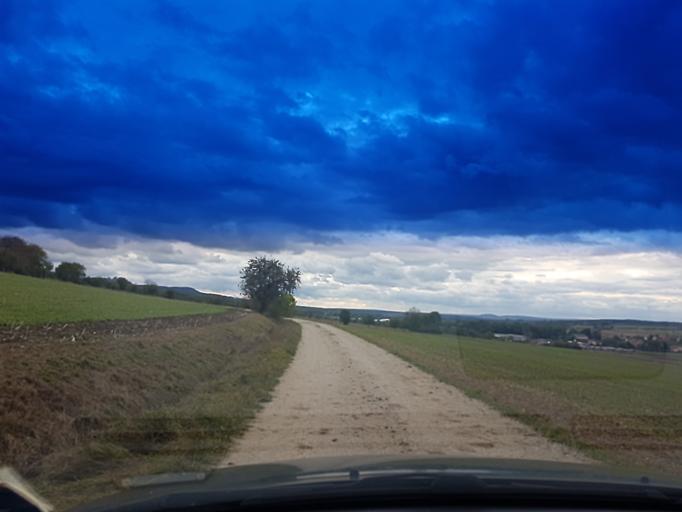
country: DE
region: Bavaria
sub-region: Upper Franconia
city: Schesslitz
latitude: 49.9945
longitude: 11.0606
